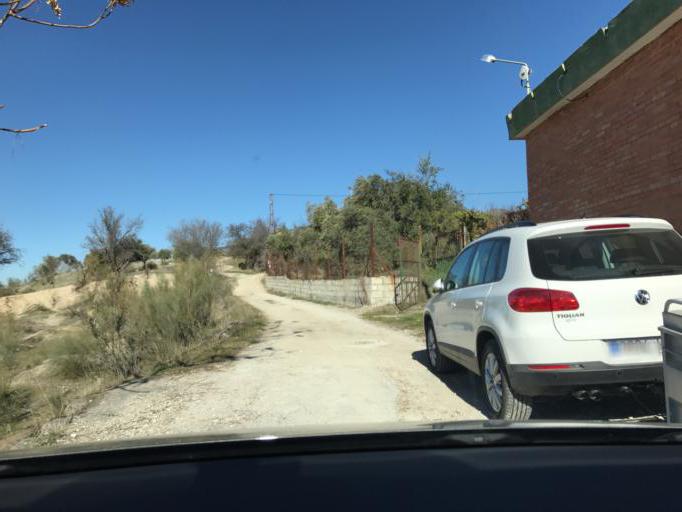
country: ES
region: Andalusia
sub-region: Provincia de Granada
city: Viznar
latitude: 37.2158
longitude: -3.5548
